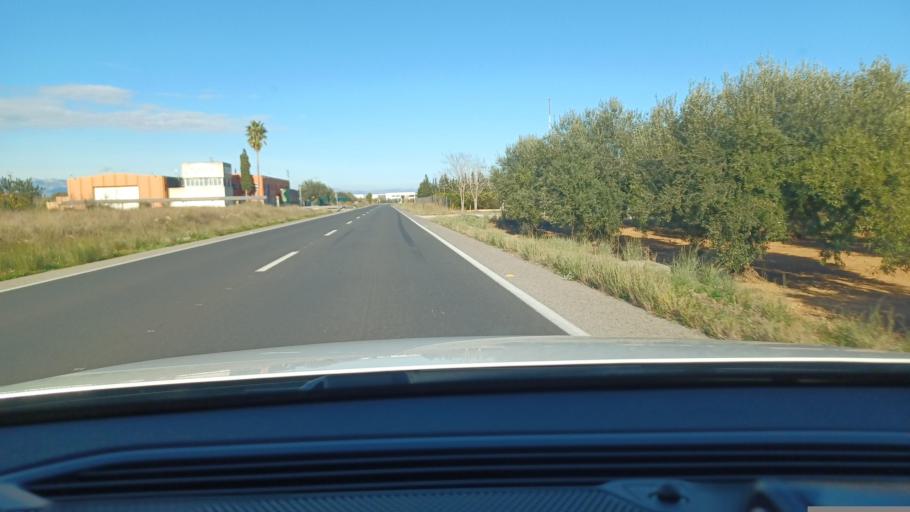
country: ES
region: Catalonia
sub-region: Provincia de Tarragona
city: Santa Barbara
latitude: 40.7308
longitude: 0.5032
